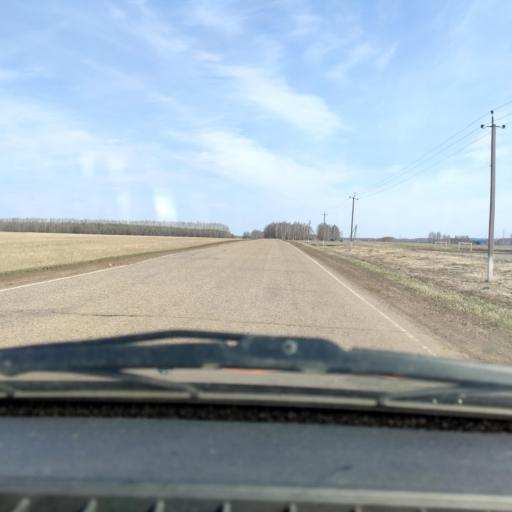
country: RU
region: Bashkortostan
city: Asanovo
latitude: 54.7911
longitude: 55.5200
